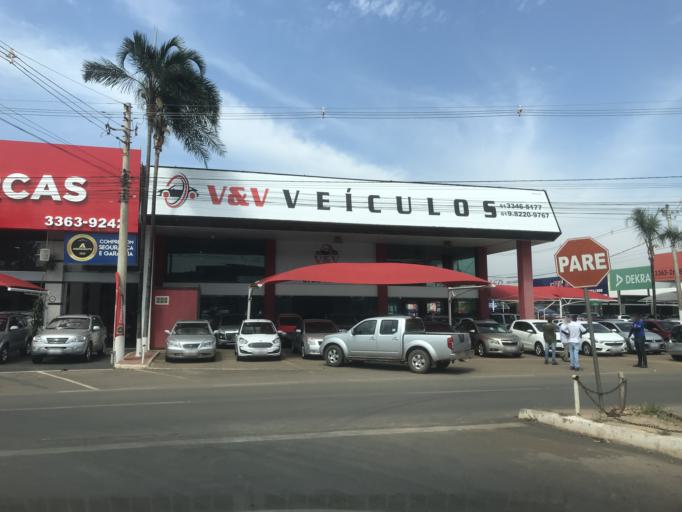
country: BR
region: Federal District
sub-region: Brasilia
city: Brasilia
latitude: -15.7913
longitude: -47.9717
